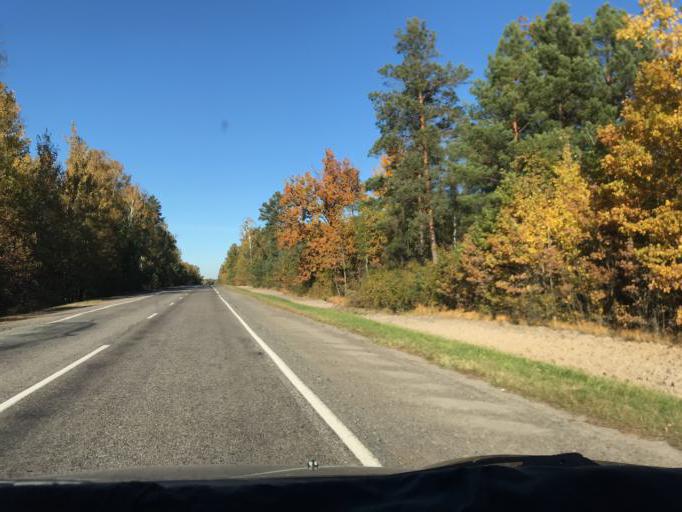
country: BY
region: Gomel
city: Yel'sk
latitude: 51.7225
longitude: 29.1714
